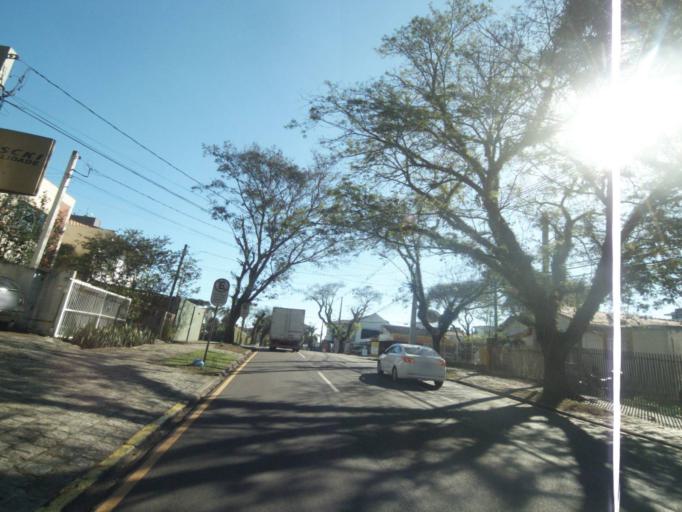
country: BR
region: Parana
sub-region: Curitiba
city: Curitiba
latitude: -25.4009
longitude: -49.2413
